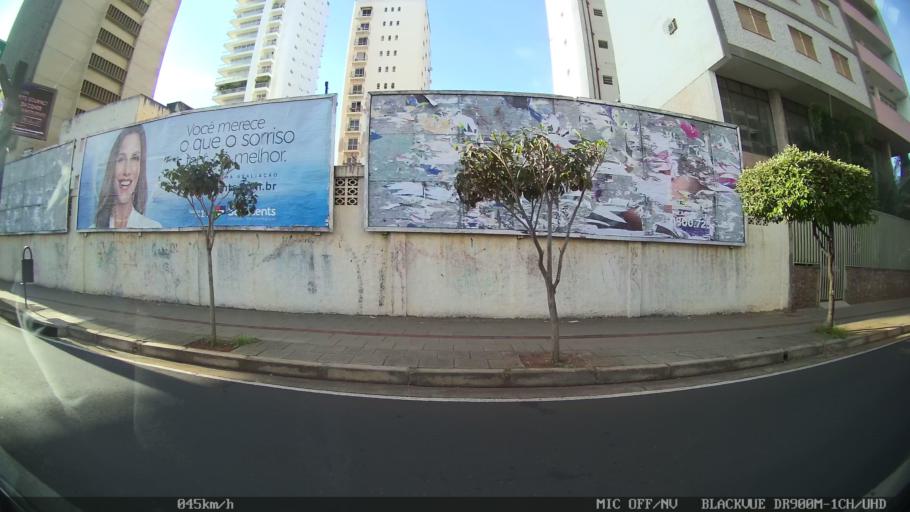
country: BR
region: Sao Paulo
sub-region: Sao Jose Do Rio Preto
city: Sao Jose do Rio Preto
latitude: -20.8135
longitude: -49.3771
